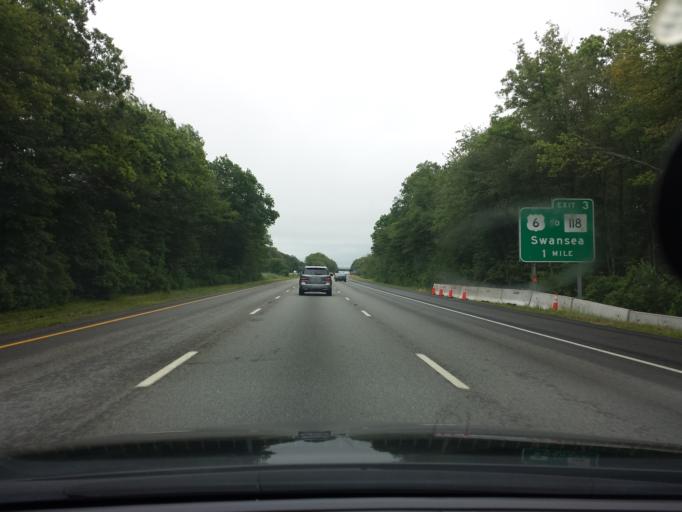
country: US
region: Massachusetts
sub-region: Bristol County
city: Ocean Grove
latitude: 41.7607
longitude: -71.2306
